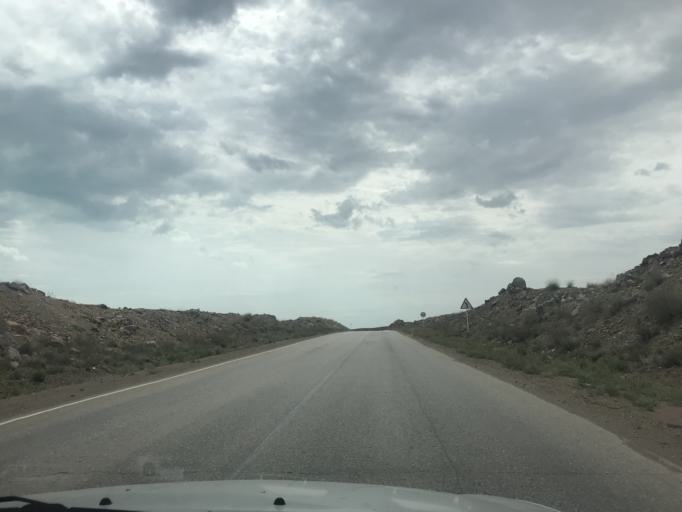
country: KZ
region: Zhambyl
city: Mynaral
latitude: 45.5088
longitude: 73.5002
